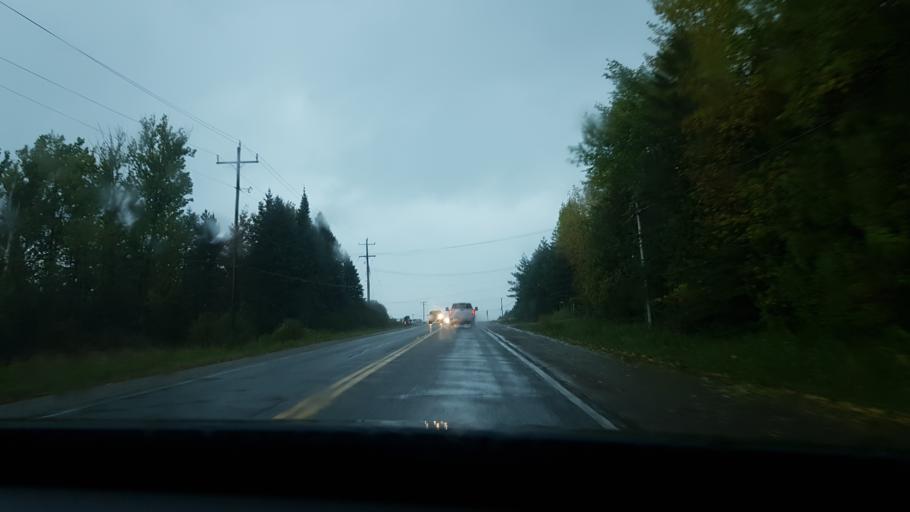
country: CA
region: Ontario
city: Peterborough
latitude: 44.3834
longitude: -78.4175
